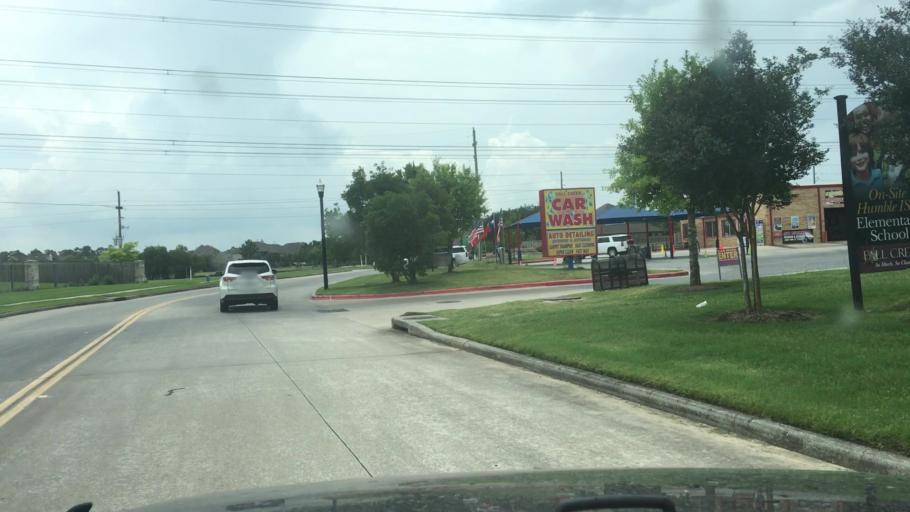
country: US
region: Texas
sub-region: Harris County
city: Humble
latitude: 29.9330
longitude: -95.2459
